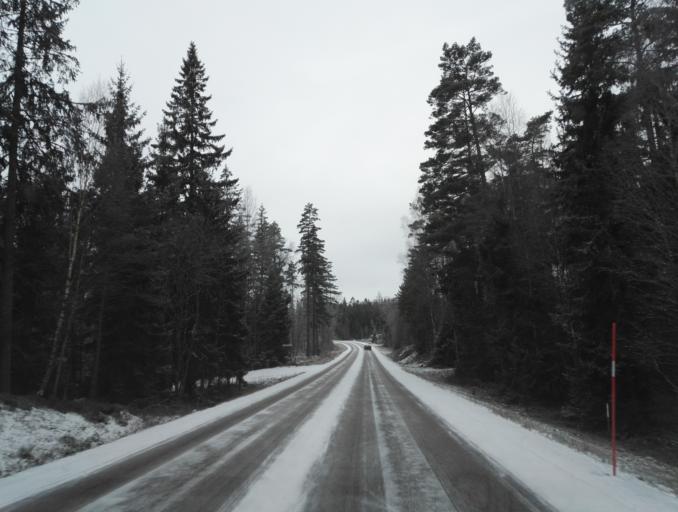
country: SE
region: Kronoberg
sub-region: Lessebo Kommun
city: Lessebo
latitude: 56.8049
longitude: 15.3549
